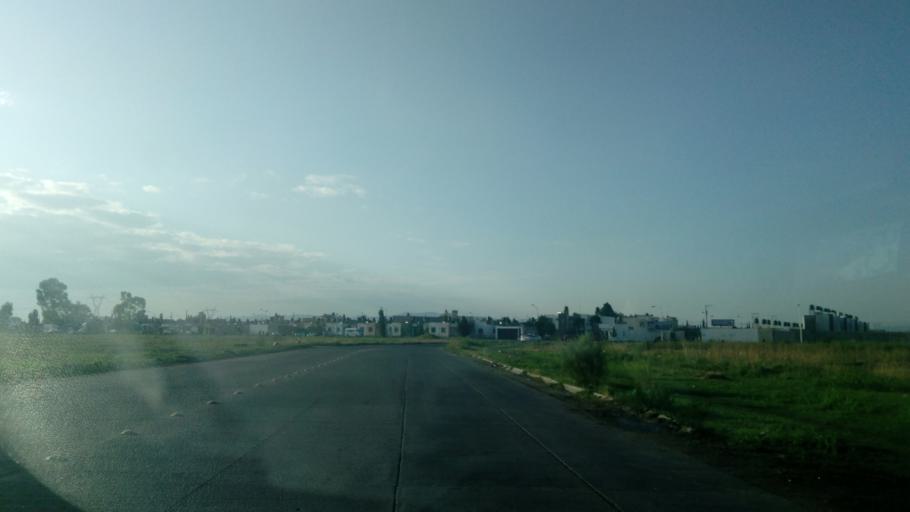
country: MX
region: Durango
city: Victoria de Durango
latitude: 24.0746
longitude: -104.5909
